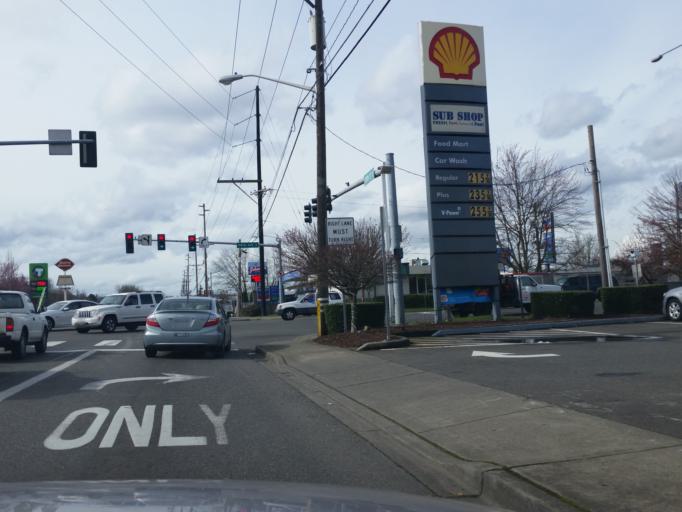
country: US
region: Washington
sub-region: Pierce County
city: Fife
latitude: 47.2390
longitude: -122.3565
